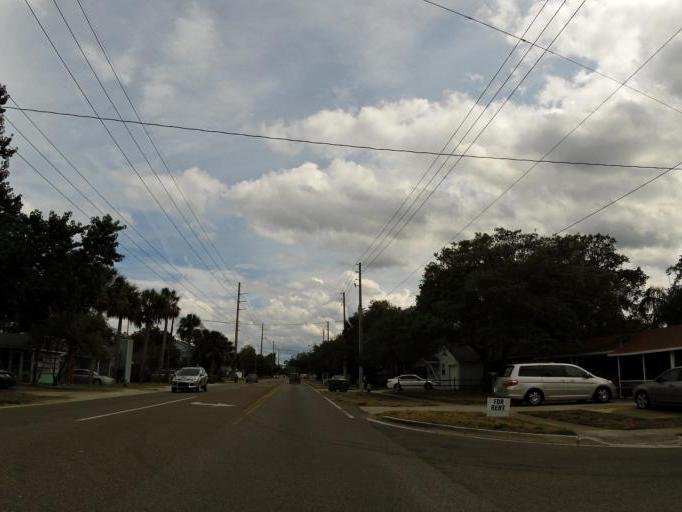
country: US
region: Florida
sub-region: Duval County
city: Jacksonville Beach
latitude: 30.2993
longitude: -81.4066
